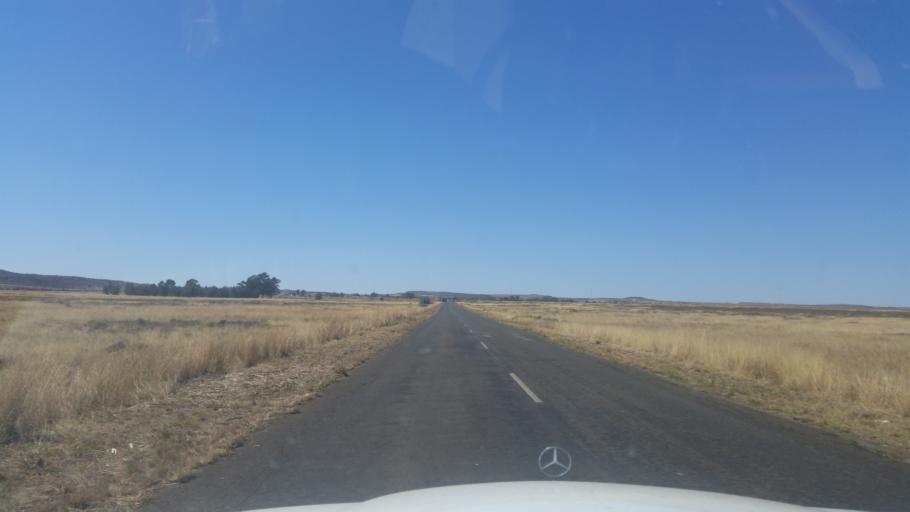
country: ZA
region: Eastern Cape
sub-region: Joe Gqabi District Municipality
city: Burgersdorp
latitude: -30.7590
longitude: 25.7795
